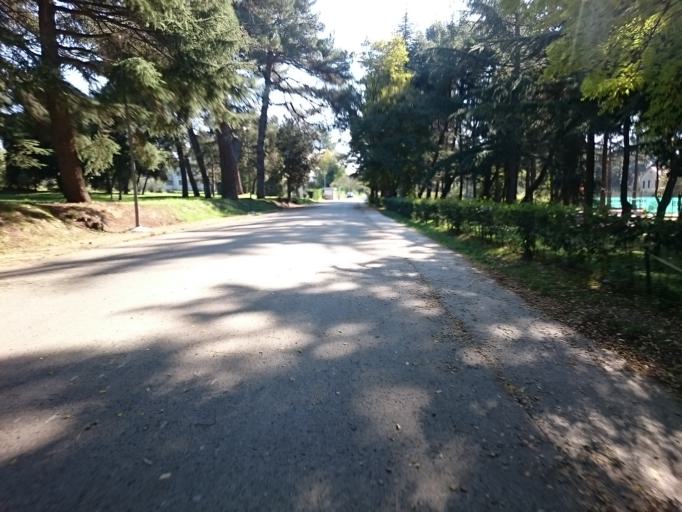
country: HR
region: Istarska
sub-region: Grad Porec
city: Porec
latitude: 45.2357
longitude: 13.5974
